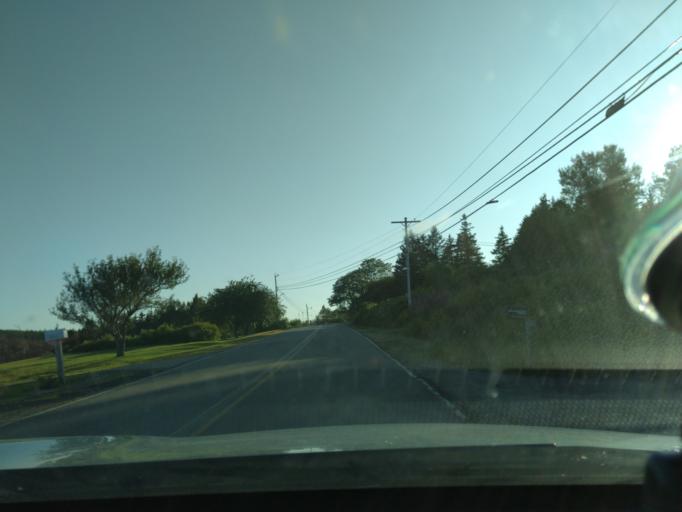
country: US
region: Maine
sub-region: Washington County
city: Machiasport
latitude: 44.6610
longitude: -67.2282
